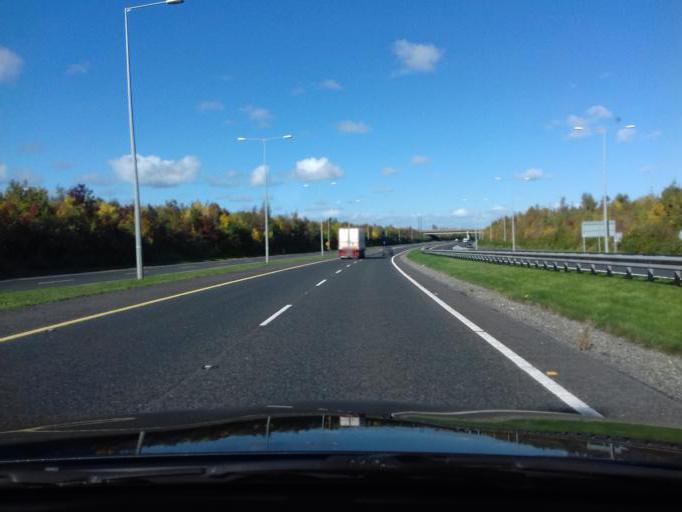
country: IE
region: Leinster
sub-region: Fingal County
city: Blanchardstown
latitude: 53.4351
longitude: -6.3501
